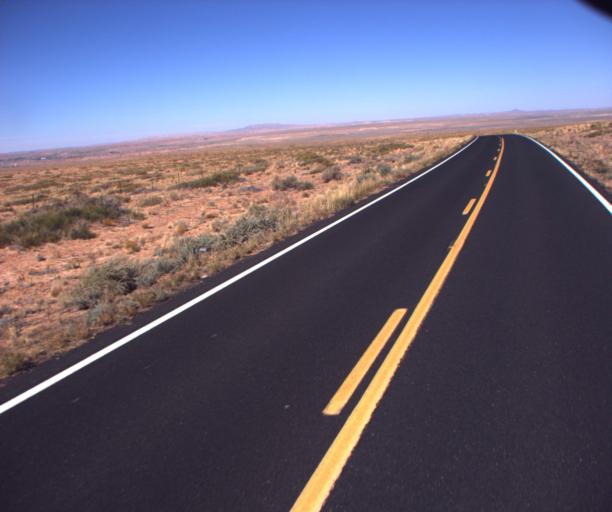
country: US
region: Arizona
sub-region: Coconino County
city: Tuba City
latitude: 36.0467
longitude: -111.1821
